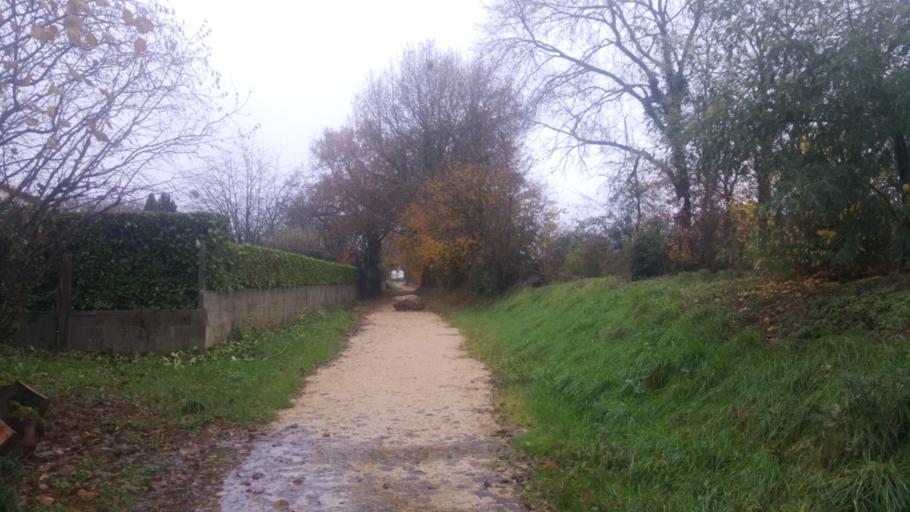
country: FR
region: Poitou-Charentes
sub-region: Departement des Deux-Sevres
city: Melle
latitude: 46.2317
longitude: -0.1333
